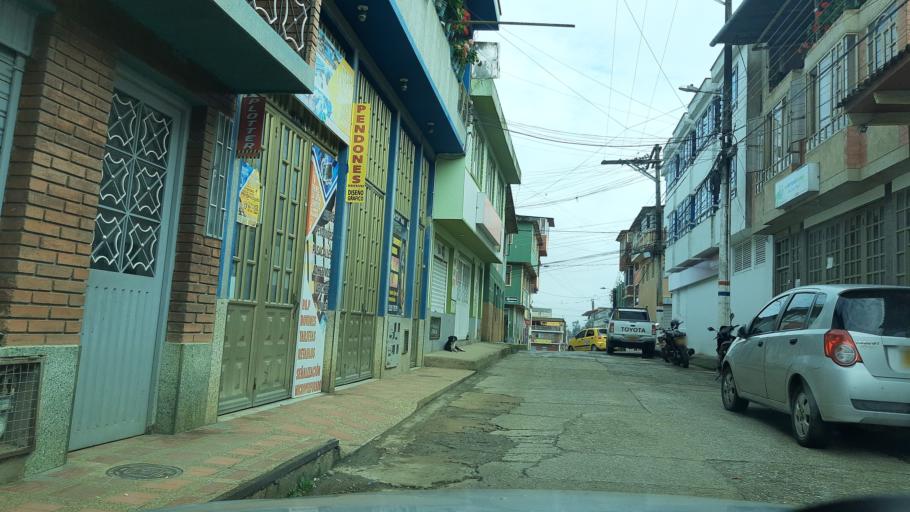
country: CO
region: Boyaca
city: Garagoa
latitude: 5.0815
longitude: -73.3650
